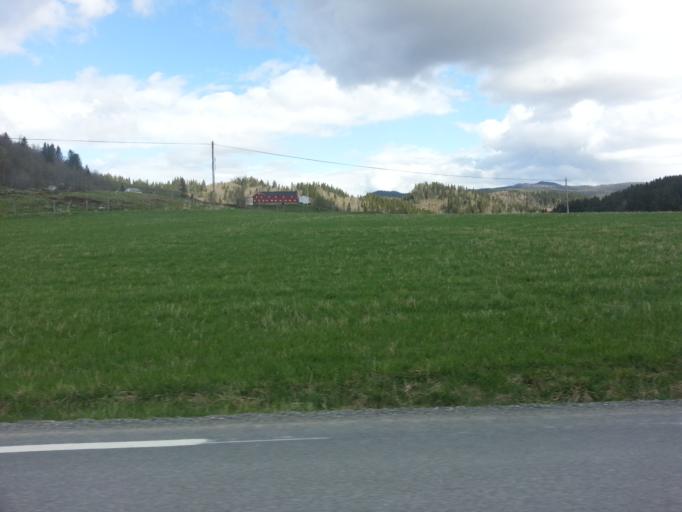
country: NO
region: Nord-Trondelag
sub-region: Levanger
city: Skogn
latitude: 63.6393
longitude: 11.2607
